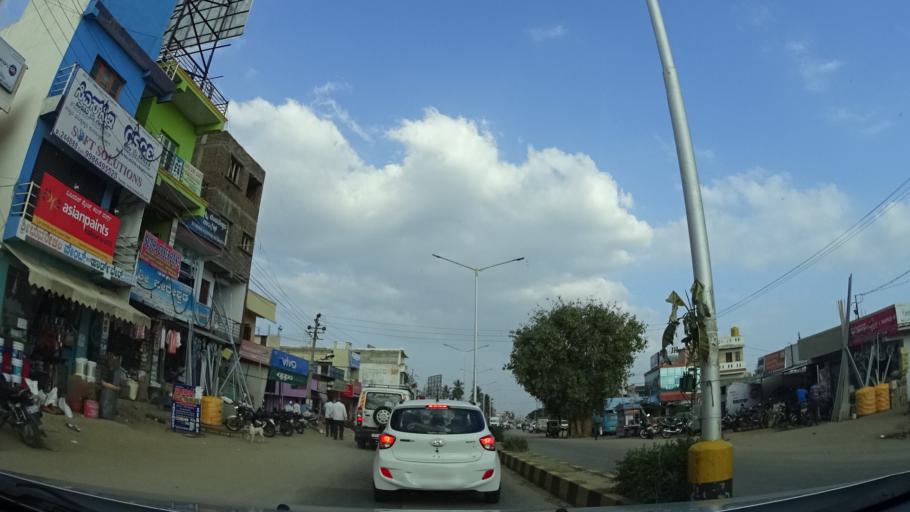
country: IN
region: Karnataka
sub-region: Mandya
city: Malavalli
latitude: 12.3851
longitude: 77.0542
